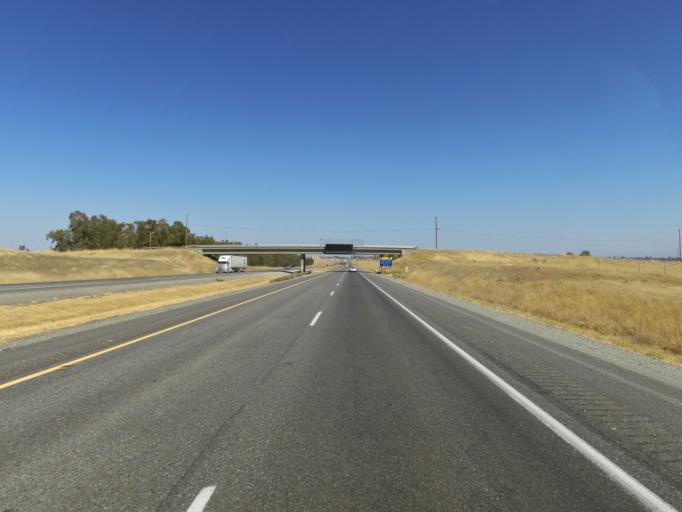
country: US
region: California
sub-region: Tehama County
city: Corning
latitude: 39.8476
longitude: -122.1998
